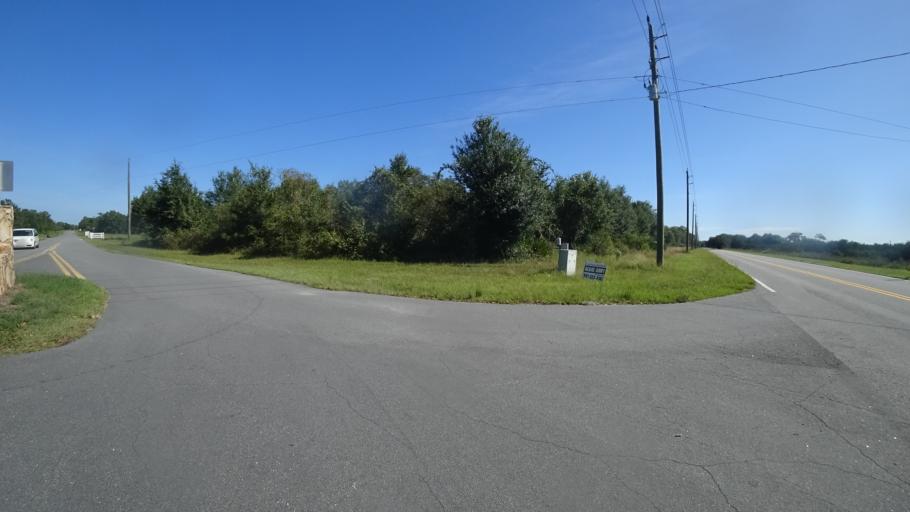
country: US
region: Florida
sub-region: Sarasota County
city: Lake Sarasota
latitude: 27.3503
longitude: -82.2509
